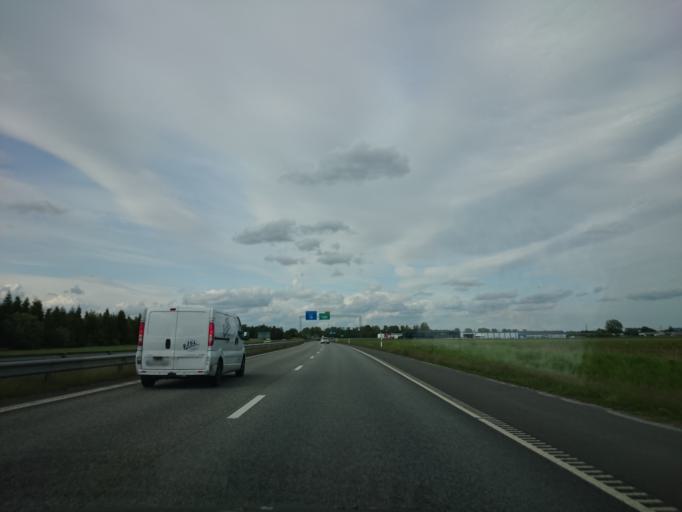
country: SE
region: Skane
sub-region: Kristianstads Kommun
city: Norra Asum
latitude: 56.0072
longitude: 14.1080
